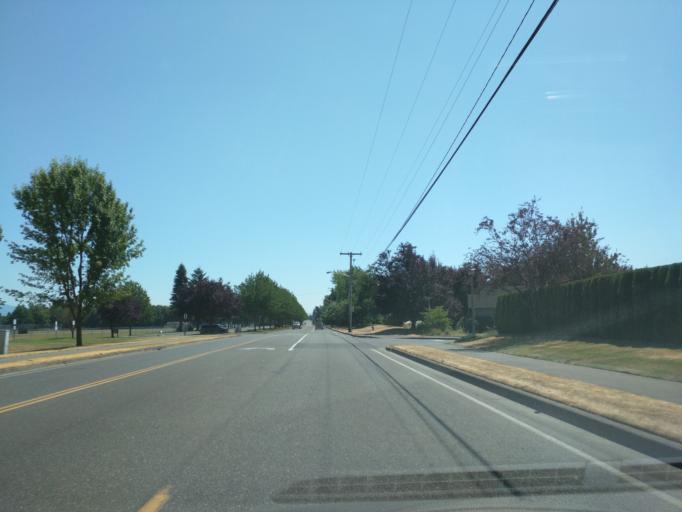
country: US
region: Washington
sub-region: Whatcom County
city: Lynden
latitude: 48.9604
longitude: -122.4413
